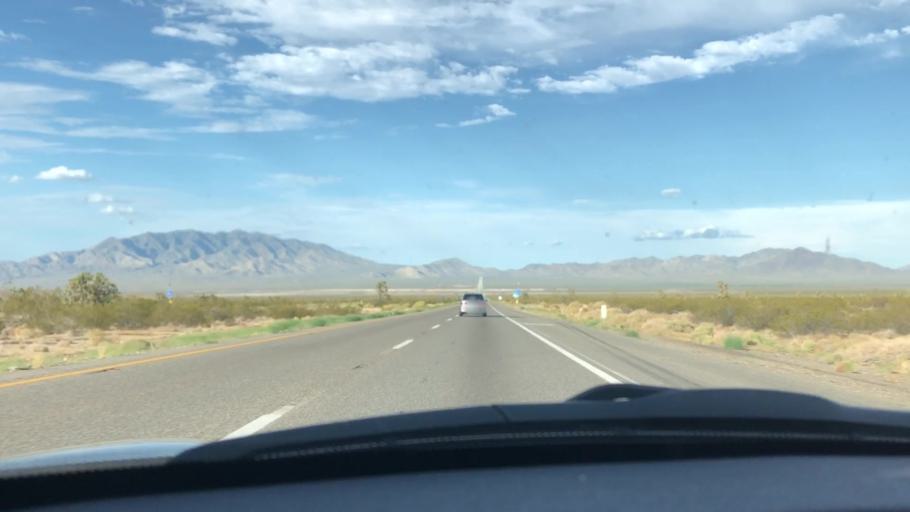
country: US
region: Nevada
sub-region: Clark County
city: Sandy Valley
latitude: 35.4163
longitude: -115.7524
